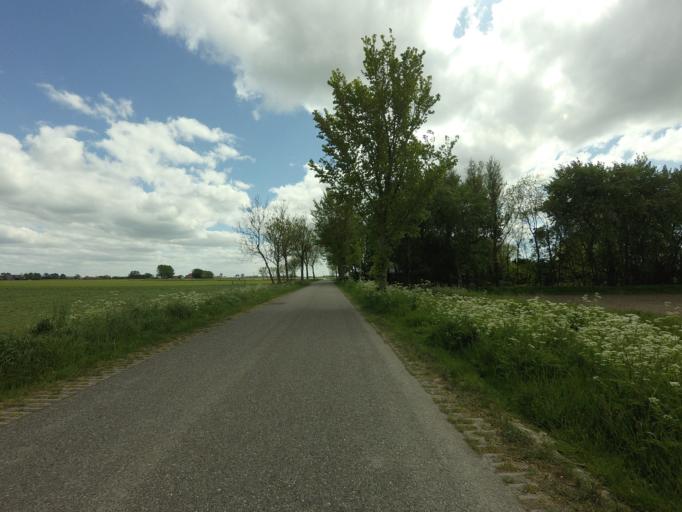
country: NL
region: Friesland
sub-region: Sudwest Fryslan
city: Bolsward
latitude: 53.0849
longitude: 5.5481
